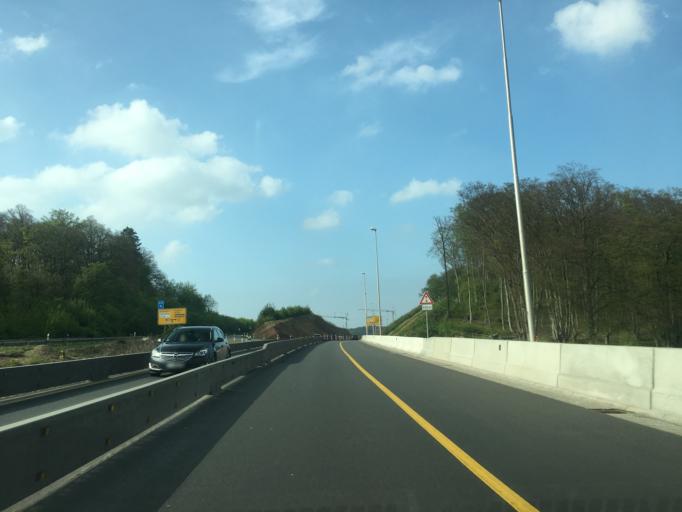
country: DE
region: Lower Saxony
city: Belm
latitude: 52.2933
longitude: 8.1072
